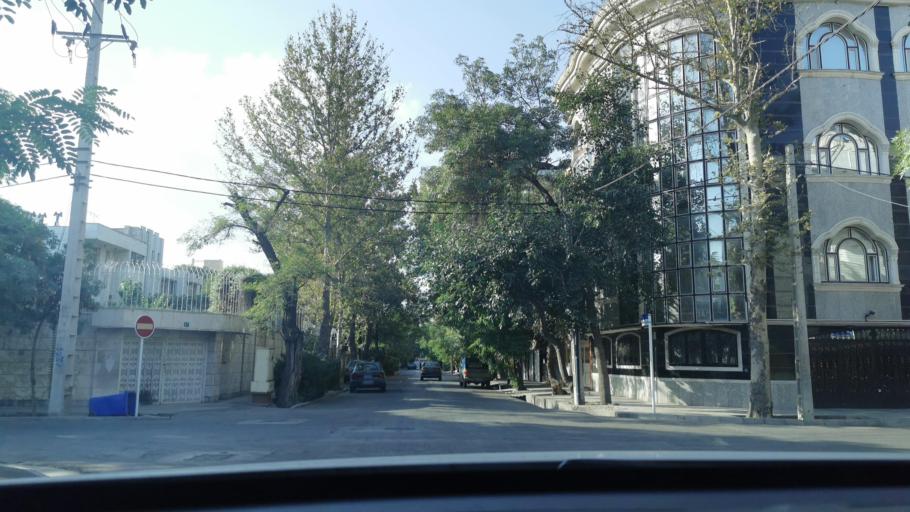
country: IR
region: Razavi Khorasan
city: Mashhad
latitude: 36.2945
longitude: 59.5842
